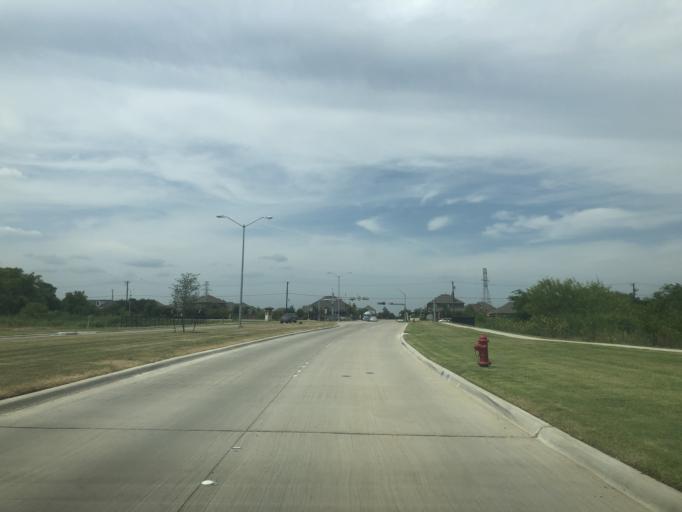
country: US
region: Texas
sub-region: Tarrant County
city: Saginaw
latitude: 32.8822
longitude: -97.3550
